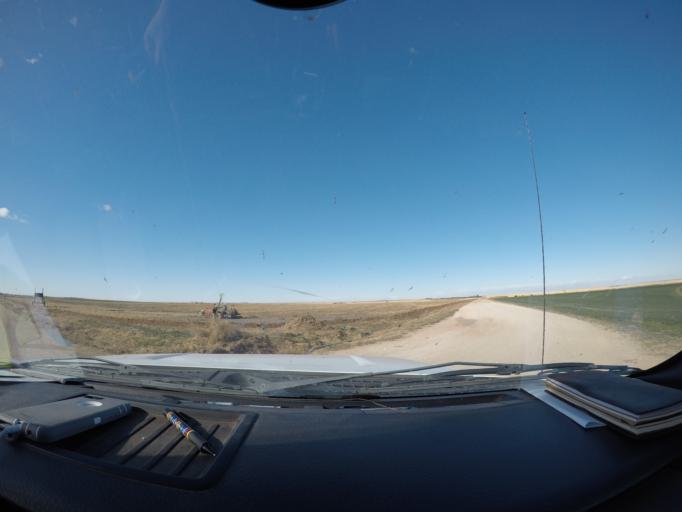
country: US
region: Texas
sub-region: Parmer County
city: Bovina
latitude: 34.5791
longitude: -103.0433
